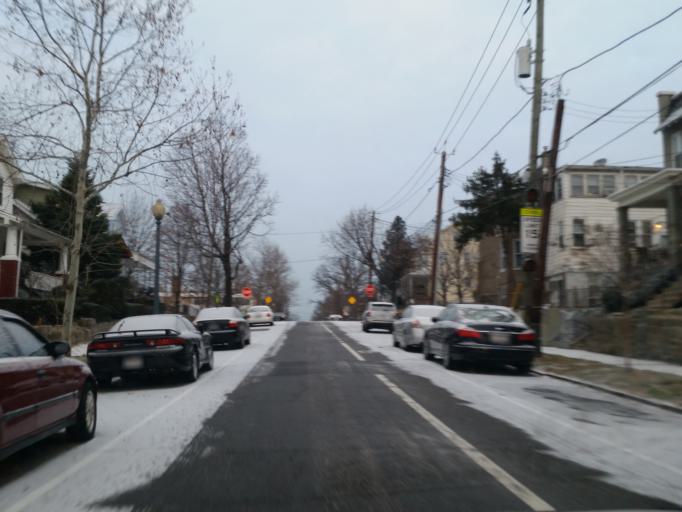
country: US
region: Maryland
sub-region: Prince George's County
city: Chillum
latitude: 38.9434
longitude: -77.0217
